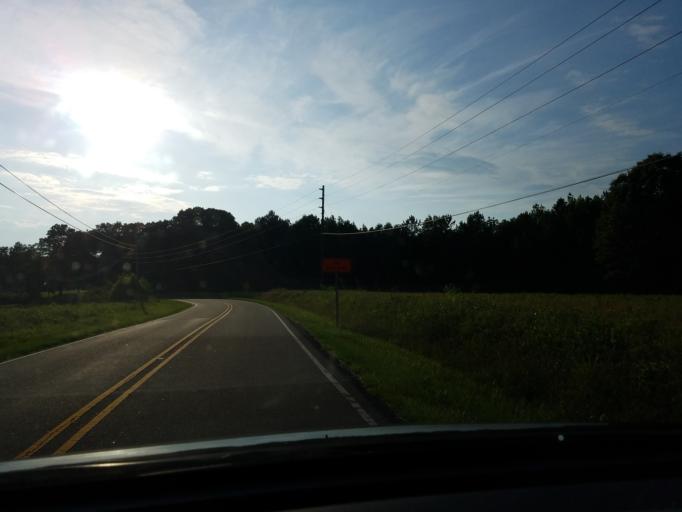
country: US
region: North Carolina
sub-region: Granville County
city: Butner
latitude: 36.1683
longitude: -78.8691
